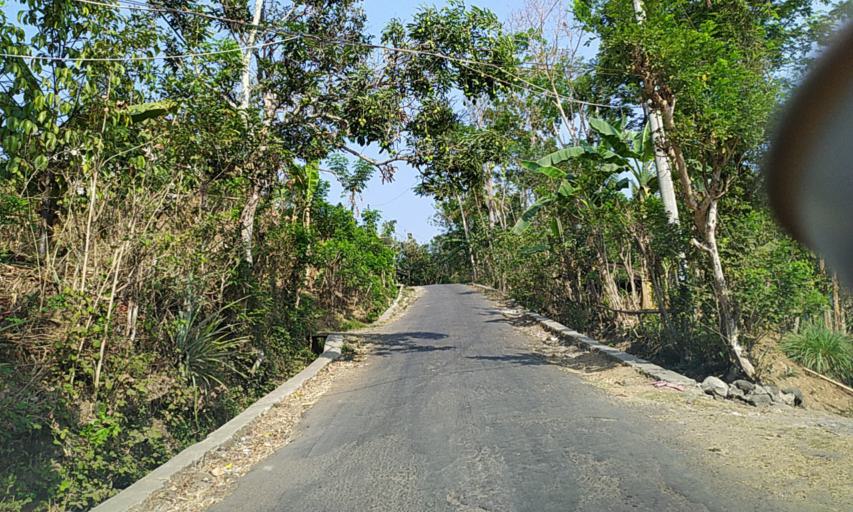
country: ID
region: Central Java
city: Cisalak
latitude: -7.3084
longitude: 108.8649
